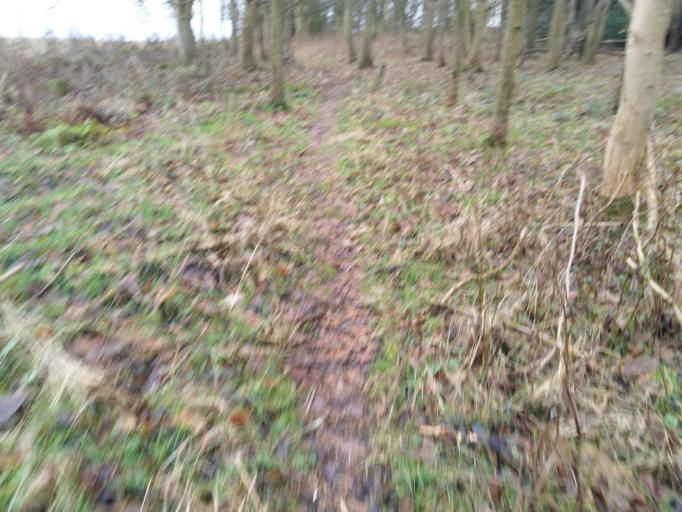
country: GB
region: Scotland
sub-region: Fife
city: Limekilns
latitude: 55.9944
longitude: -3.5115
